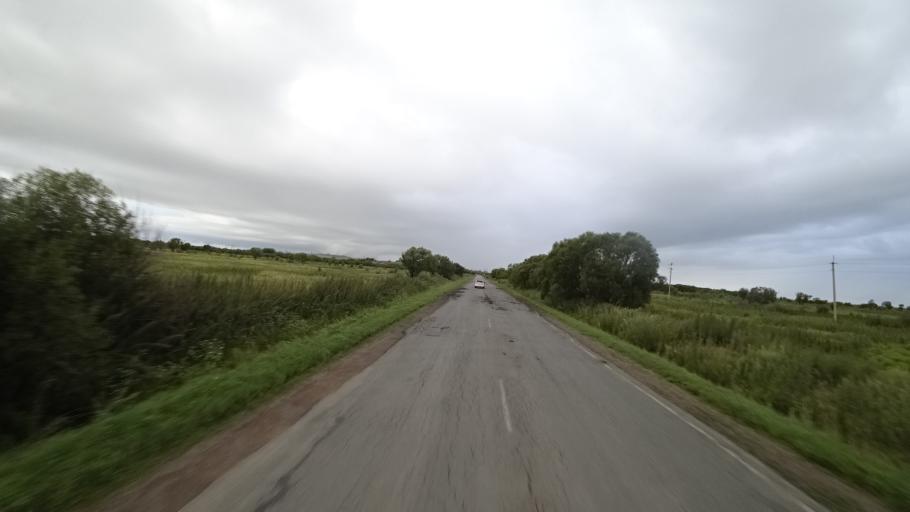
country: RU
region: Primorskiy
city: Chernigovka
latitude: 44.3596
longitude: 132.5572
